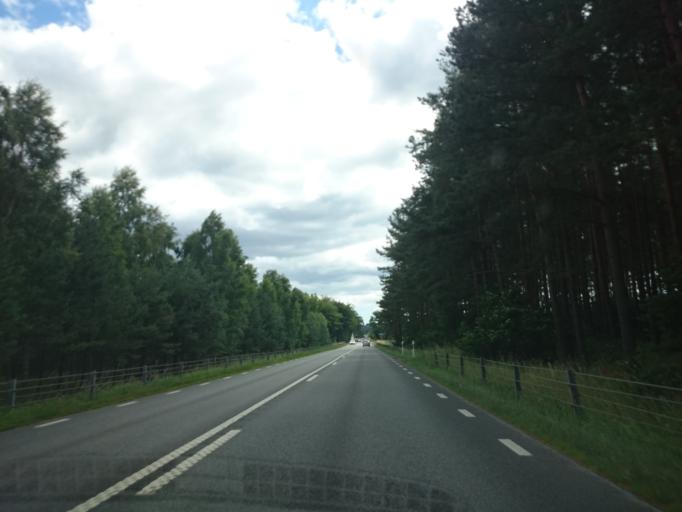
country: SE
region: Skane
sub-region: Kristianstads Kommun
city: Degeberga
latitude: 55.8162
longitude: 14.1306
